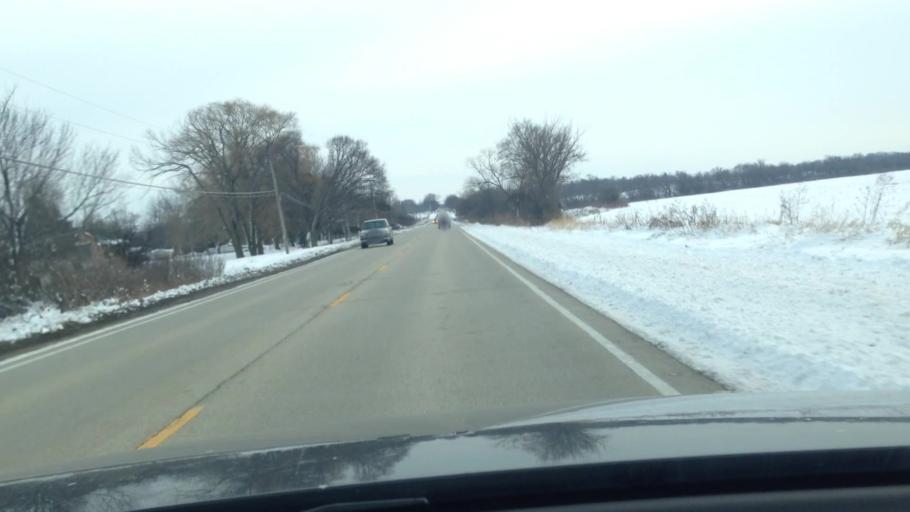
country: US
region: Illinois
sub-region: McHenry County
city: Woodstock
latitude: 42.3737
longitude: -88.4432
